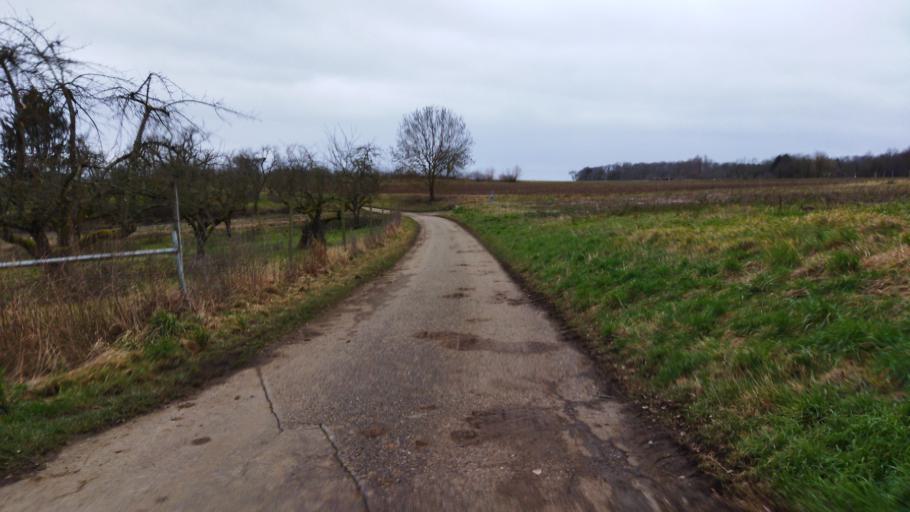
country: DE
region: Baden-Wuerttemberg
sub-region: Regierungsbezirk Stuttgart
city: Untergruppenbach
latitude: 49.0999
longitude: 9.2630
